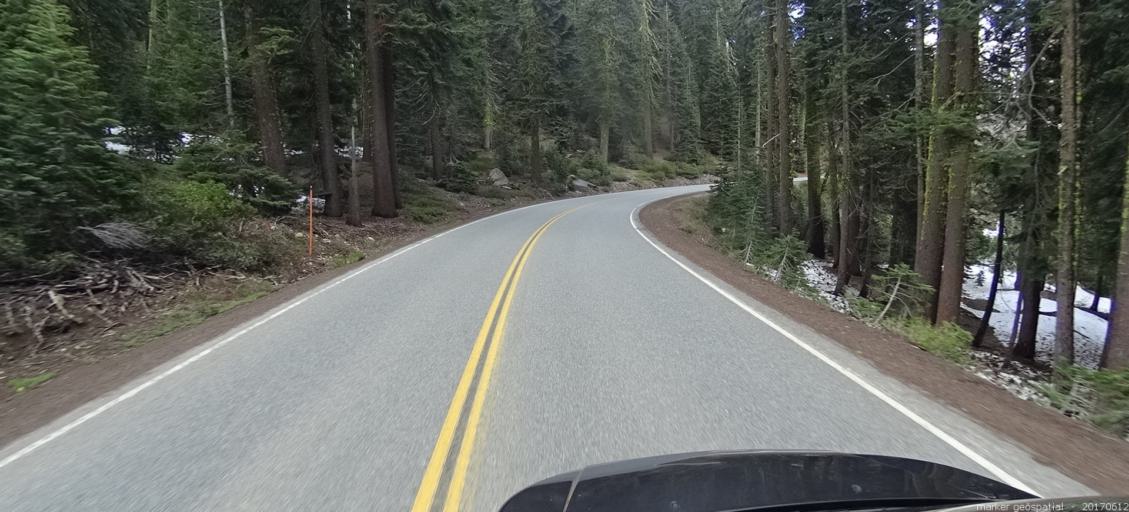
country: US
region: California
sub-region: Siskiyou County
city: Mount Shasta
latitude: 41.3459
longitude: -122.2490
